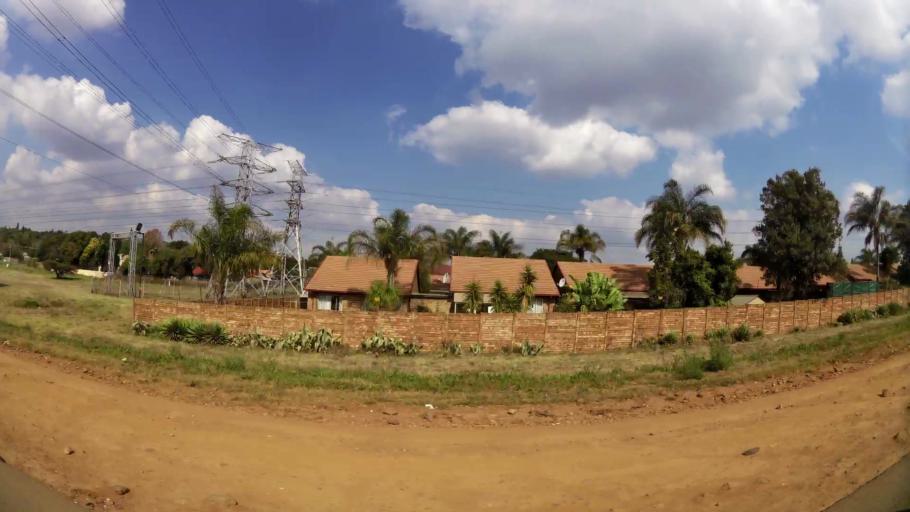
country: ZA
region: Gauteng
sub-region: City of Tshwane Metropolitan Municipality
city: Centurion
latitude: -25.8215
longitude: 28.2629
